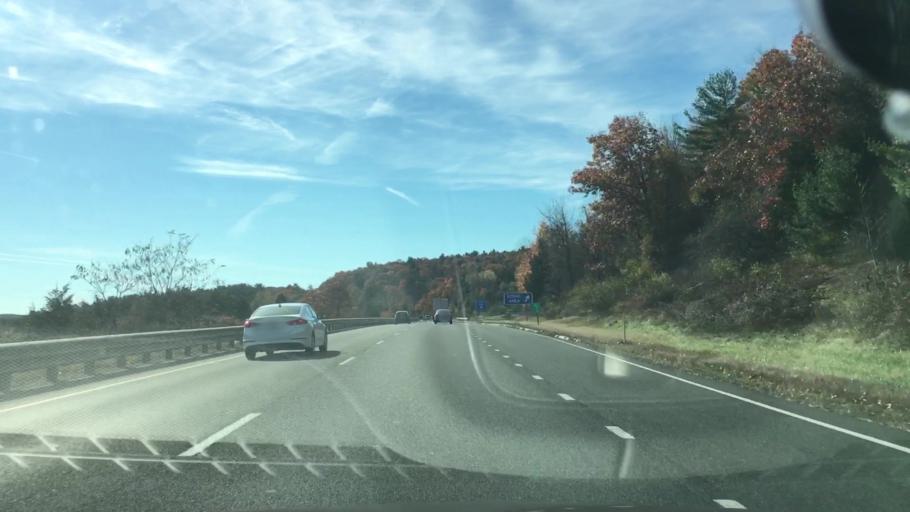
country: US
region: Massachusetts
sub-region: Hampshire County
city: South Hadley
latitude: 42.2559
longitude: -72.6193
